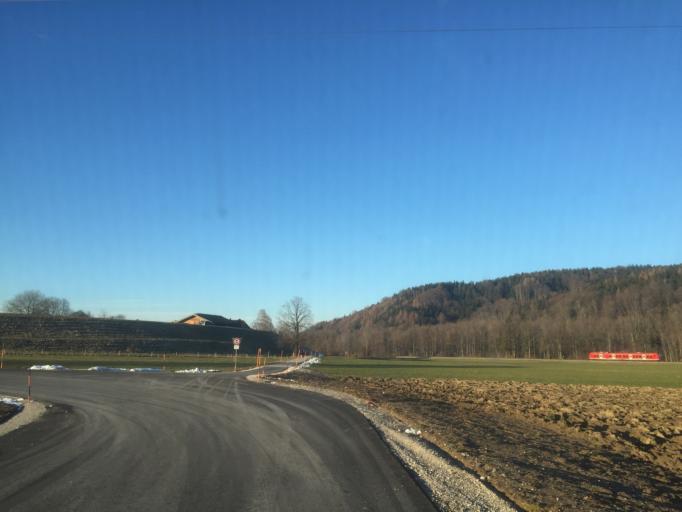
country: DE
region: Bavaria
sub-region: Upper Bavaria
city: Siegsdorf
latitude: 47.8323
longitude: 12.6418
